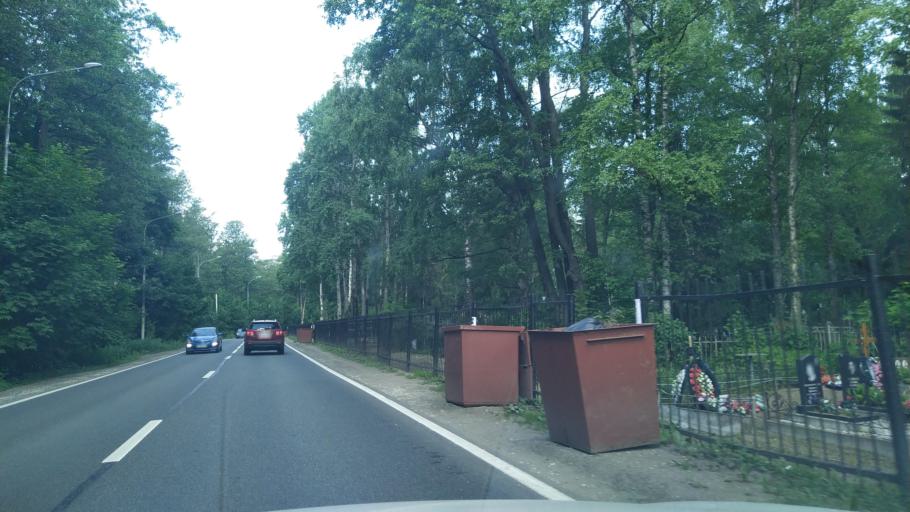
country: RU
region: St.-Petersburg
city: Kronshtadt
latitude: 60.0191
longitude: 29.7003
